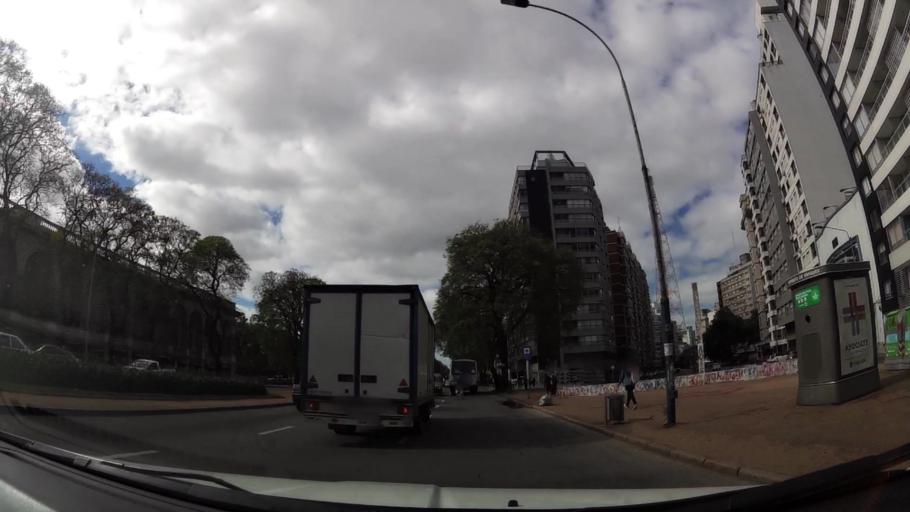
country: UY
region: Montevideo
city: Montevideo
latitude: -34.8957
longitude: -56.1649
